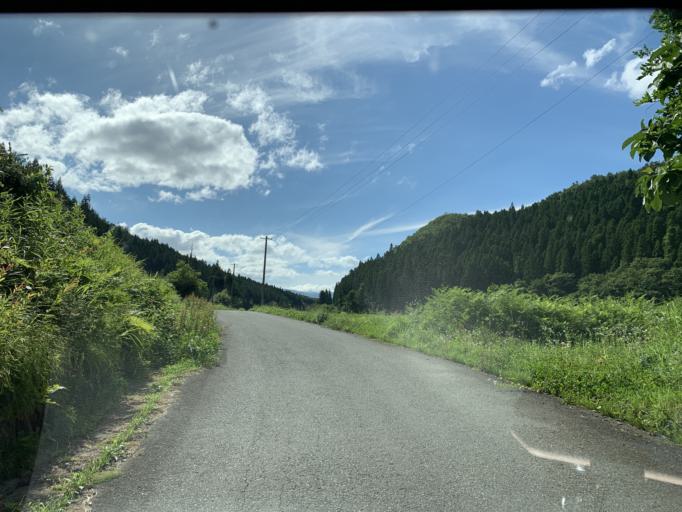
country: JP
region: Iwate
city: Ichinoseki
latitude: 38.9164
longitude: 140.9789
